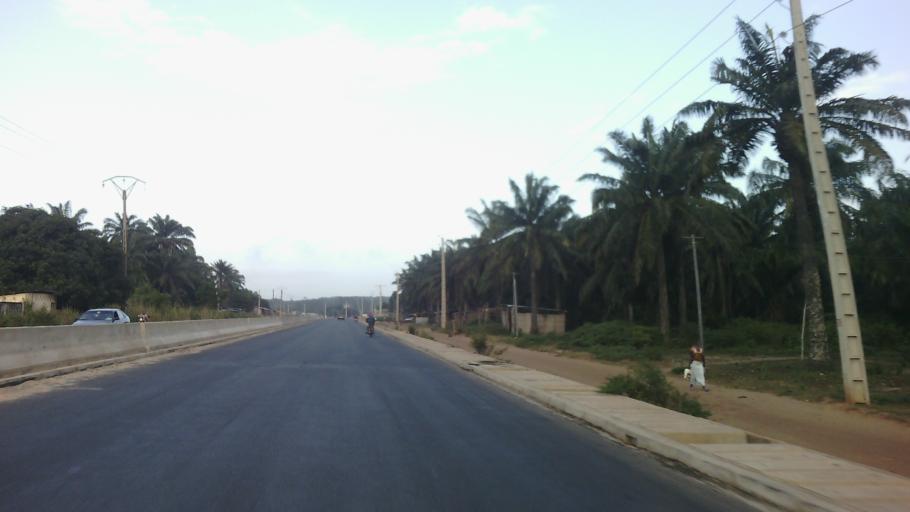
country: BJ
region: Atlantique
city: Hevie
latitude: 6.3823
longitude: 2.1754
